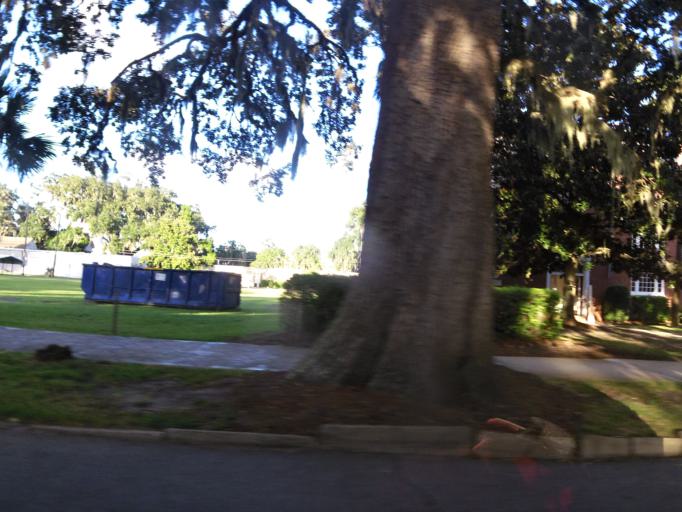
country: US
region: Georgia
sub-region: Glynn County
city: Brunswick
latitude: 31.1474
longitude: -81.4925
